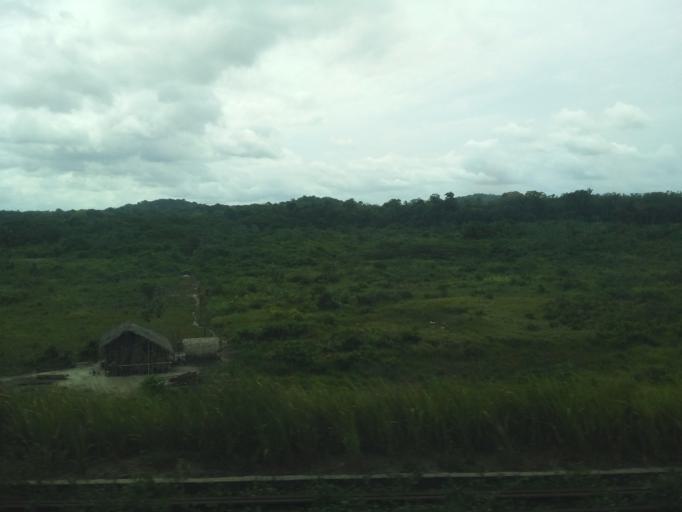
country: BR
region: Maranhao
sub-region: Santa Ines
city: Santa Ines
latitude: -3.7424
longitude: -46.1155
